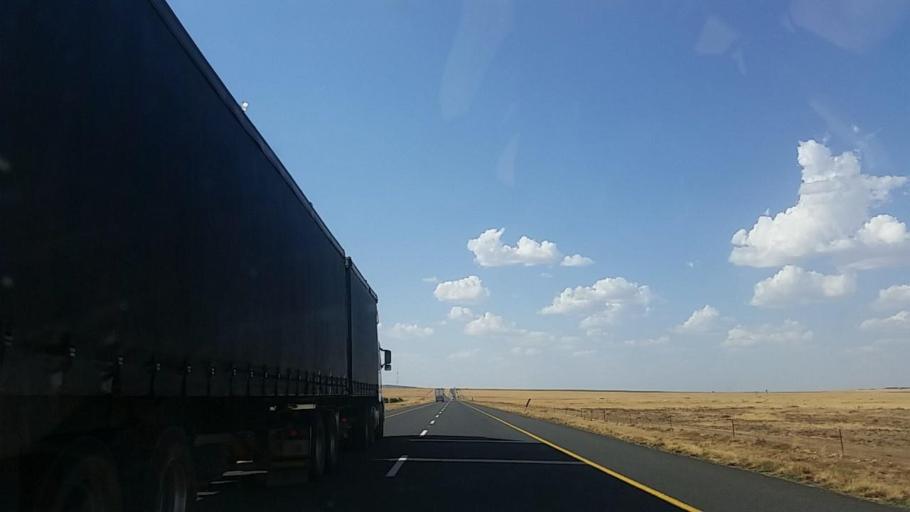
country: ZA
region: Orange Free State
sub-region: Mangaung Metropolitan Municipality
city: Bloemfontein
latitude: -29.3405
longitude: 26.1532
